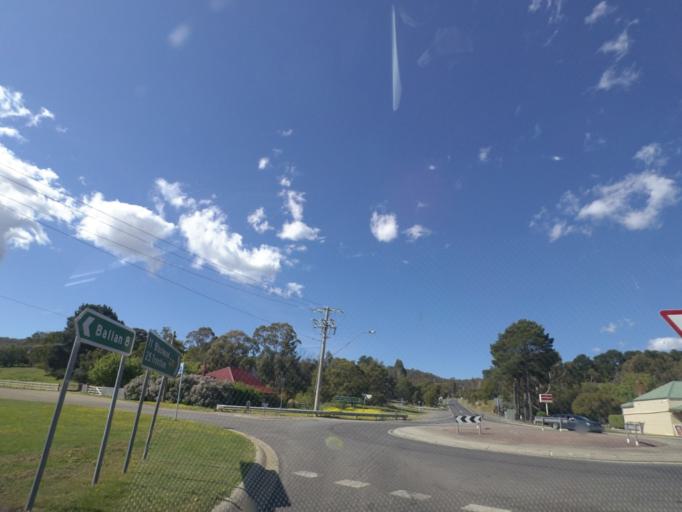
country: AU
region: Victoria
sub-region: Moorabool
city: Bacchus Marsh
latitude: -37.5608
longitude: 144.2986
